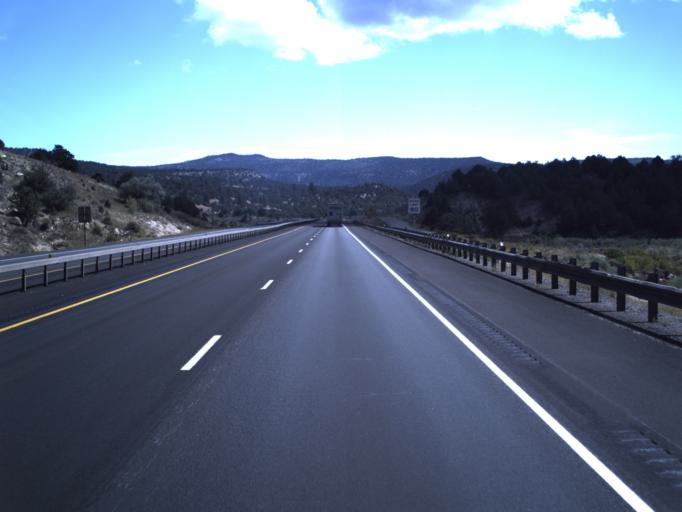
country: US
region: Utah
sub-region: Sevier County
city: Salina
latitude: 38.8818
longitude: -111.5809
